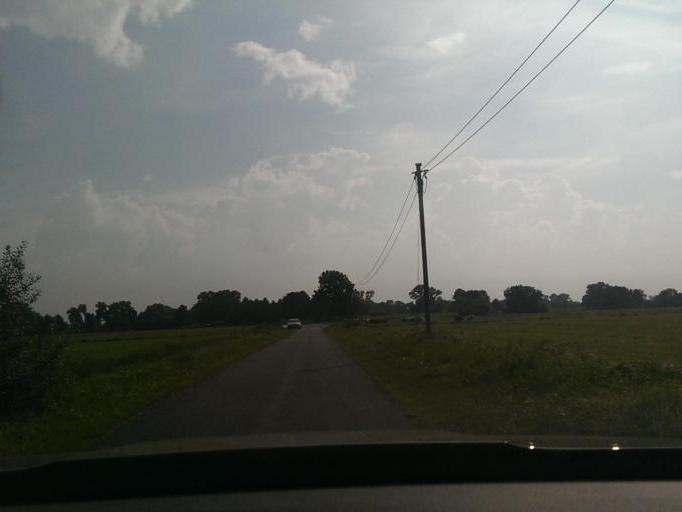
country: DE
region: Lower Saxony
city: Osterholz-Scharmbeck
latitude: 53.1671
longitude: 8.8015
